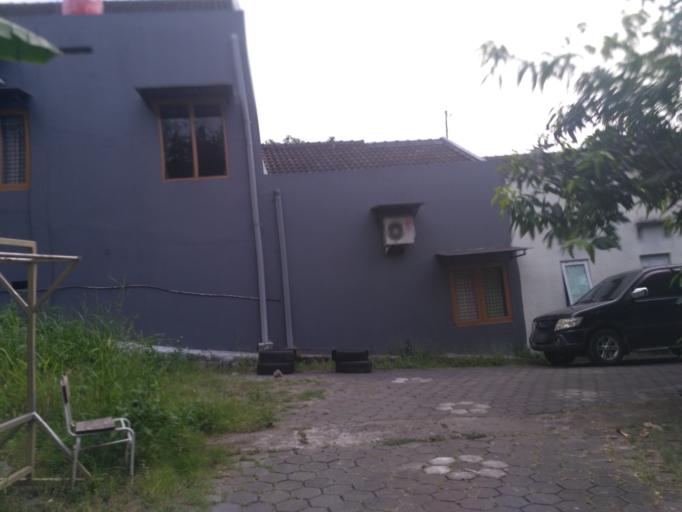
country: ID
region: Central Java
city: Mranggen
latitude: -7.0421
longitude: 110.4699
